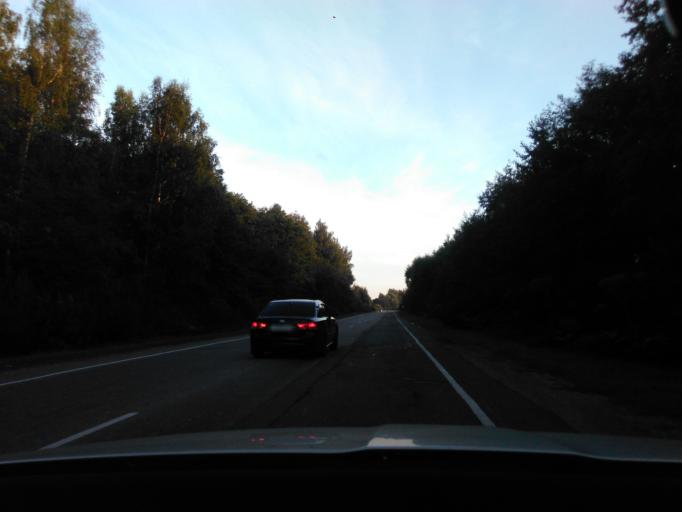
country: RU
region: Tverskaya
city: Konakovo
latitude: 56.6473
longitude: 36.7087
